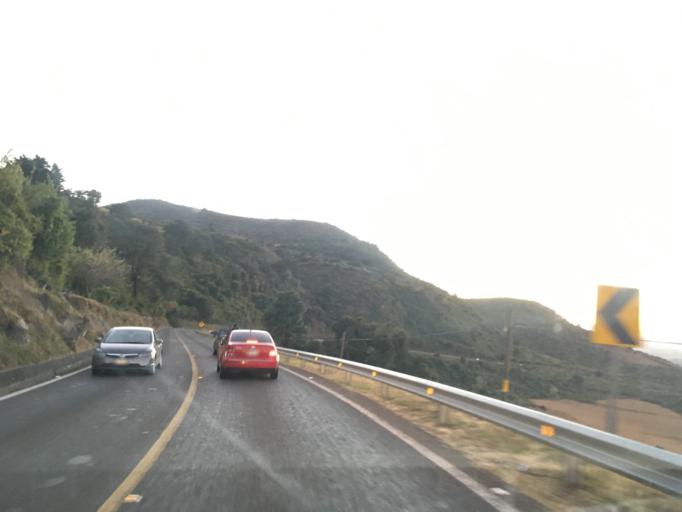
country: MX
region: Michoacan
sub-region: Zinapecuaro
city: Santa Clara del Tule
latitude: 19.8135
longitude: -100.8134
